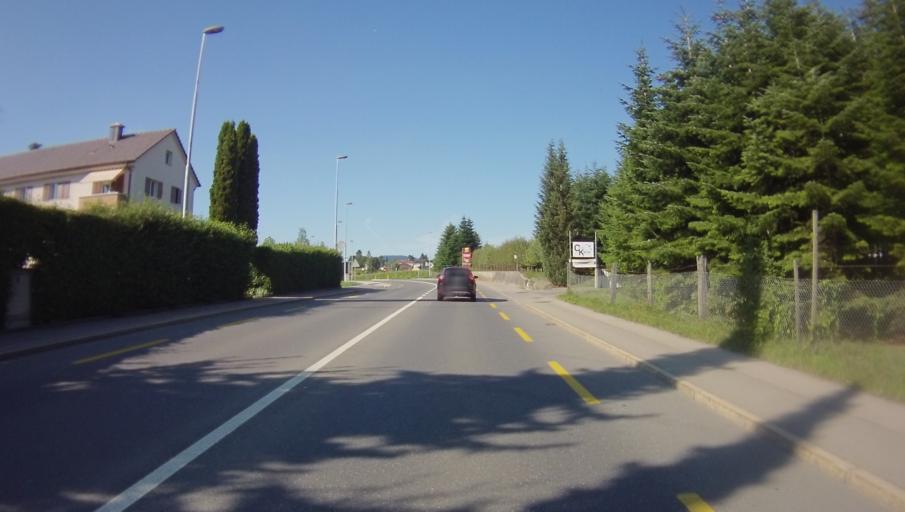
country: CH
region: Zug
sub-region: Zug
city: Steinhausen
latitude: 47.1934
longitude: 8.4760
